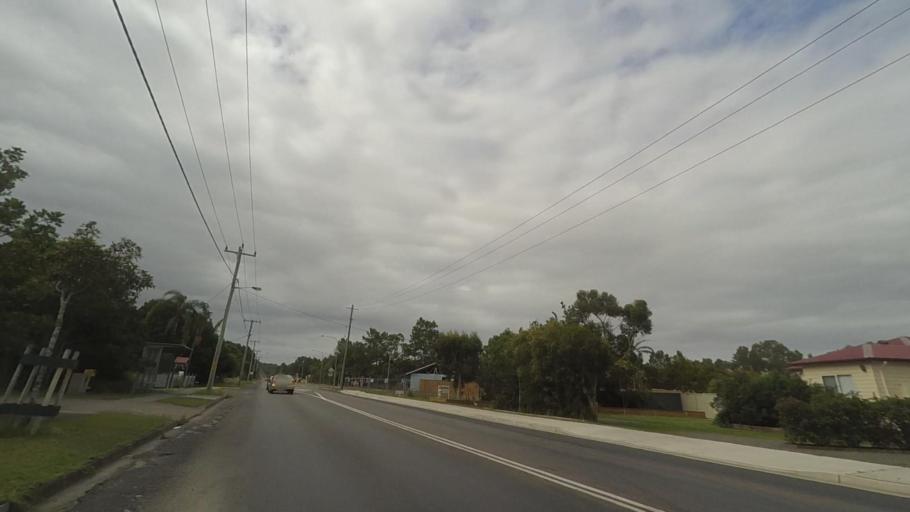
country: AU
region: New South Wales
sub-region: Great Lakes
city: Hawks Nest
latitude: -32.6538
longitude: 152.1497
